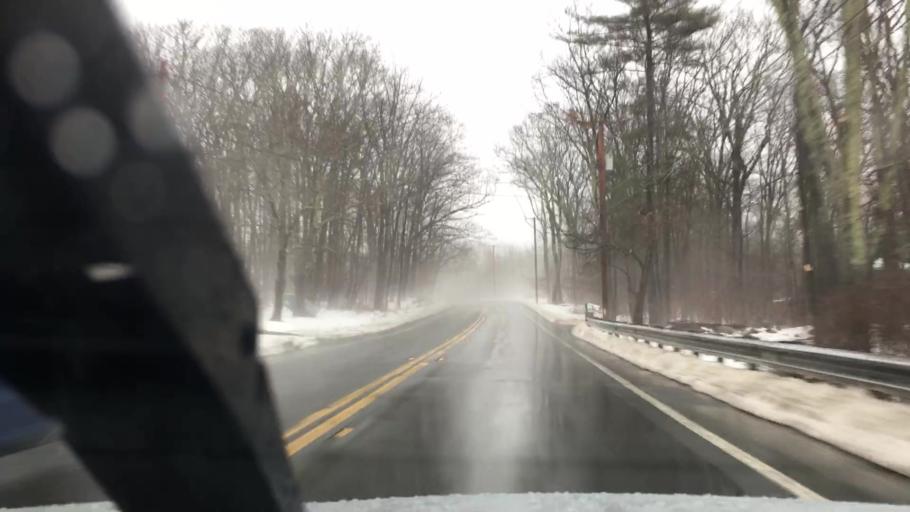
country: US
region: Massachusetts
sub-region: Hampshire County
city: Belchertown
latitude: 42.3265
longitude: -72.4032
